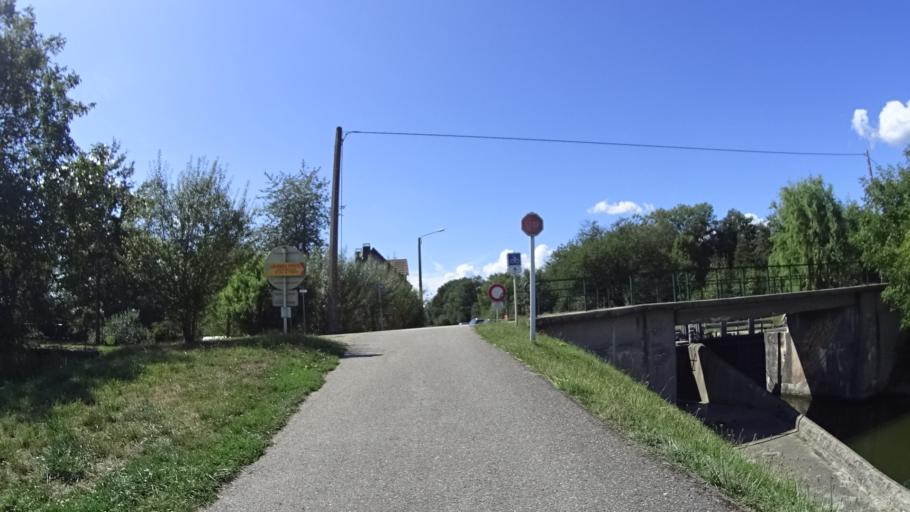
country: FR
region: Alsace
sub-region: Departement du Haut-Rhin
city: Aspach
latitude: 47.6650
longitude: 7.1969
